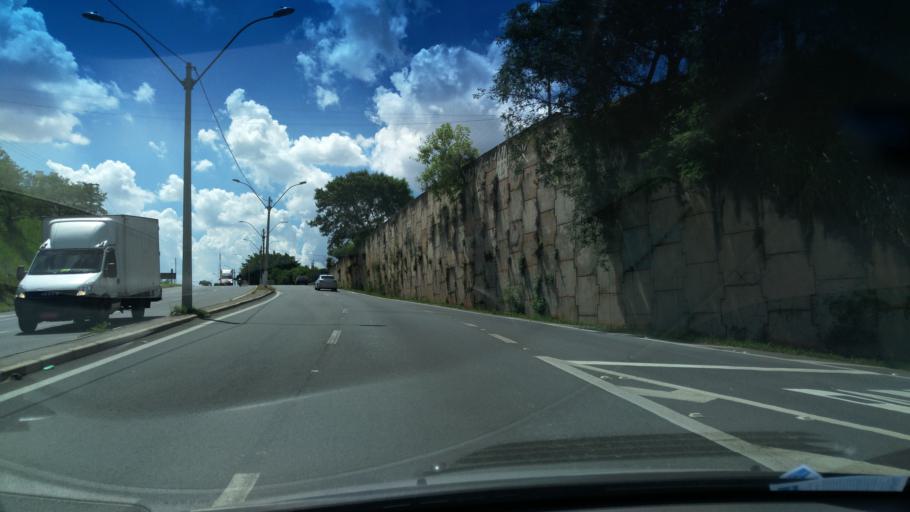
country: BR
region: Sao Paulo
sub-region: Valinhos
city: Valinhos
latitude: -22.9526
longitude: -47.0234
